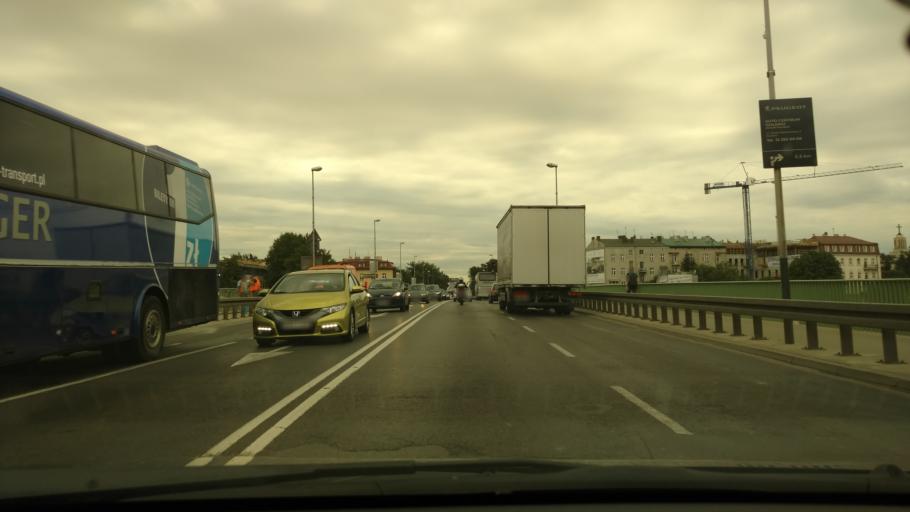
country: PL
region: Lesser Poland Voivodeship
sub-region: Krakow
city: Krakow
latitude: 50.0549
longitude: 19.9278
